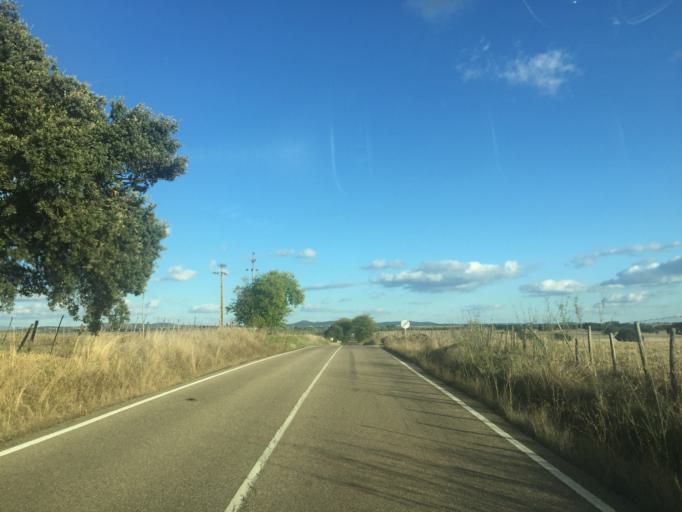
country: PT
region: Portalegre
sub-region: Alter do Chao
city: Alter do Chao
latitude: 39.2040
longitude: -7.7404
